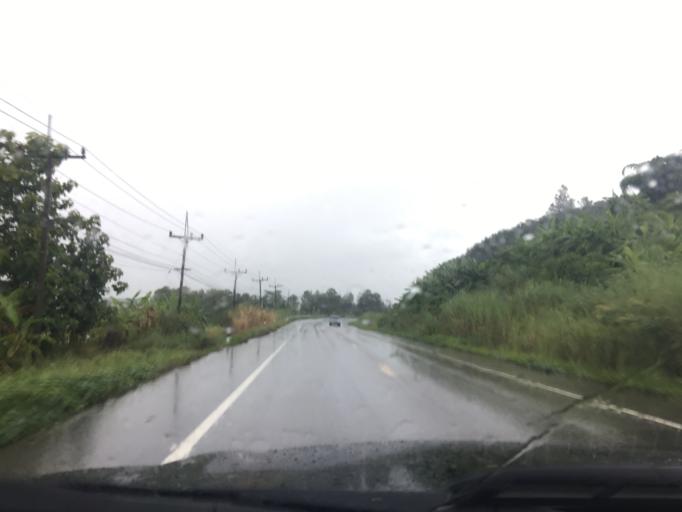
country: TH
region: Chiang Rai
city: Chiang Saen
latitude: 20.2726
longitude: 100.1985
